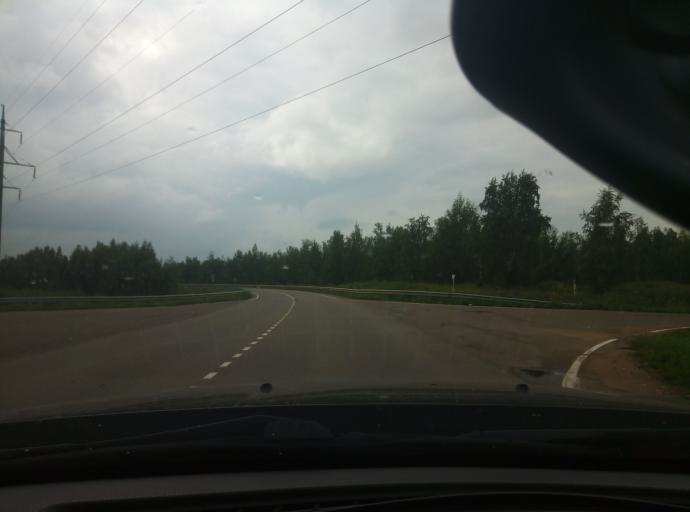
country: RU
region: Tula
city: Lomintsevskiy
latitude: 53.9424
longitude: 37.6277
